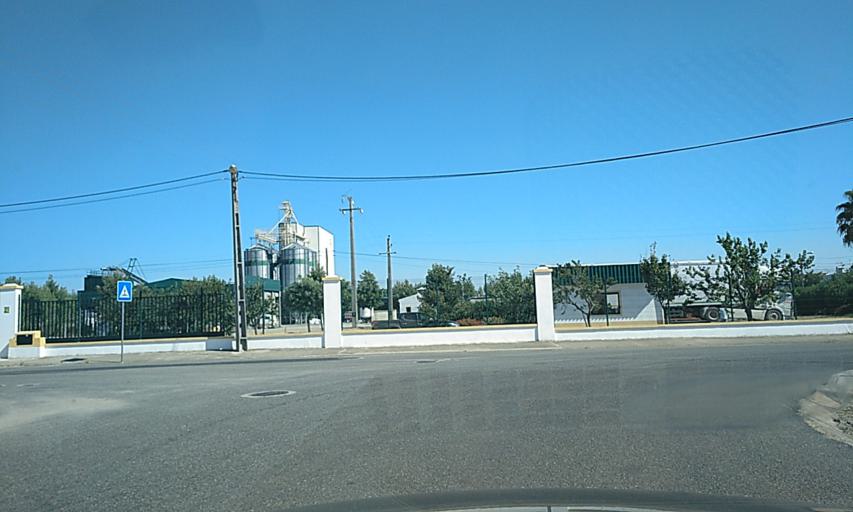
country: PT
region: Portalegre
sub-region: Campo Maior
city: Campo Maior
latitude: 39.0229
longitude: -7.0606
